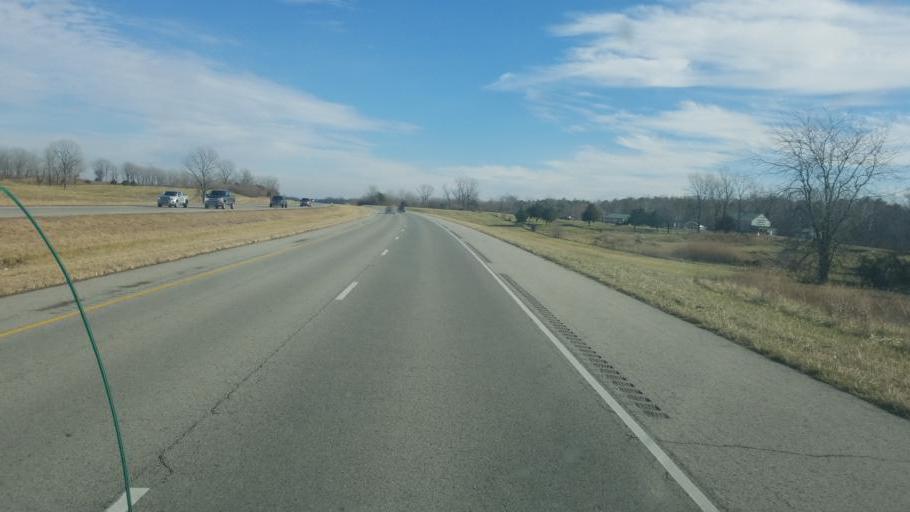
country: US
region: Illinois
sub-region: Williamson County
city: Marion
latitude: 37.7305
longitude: -88.7852
